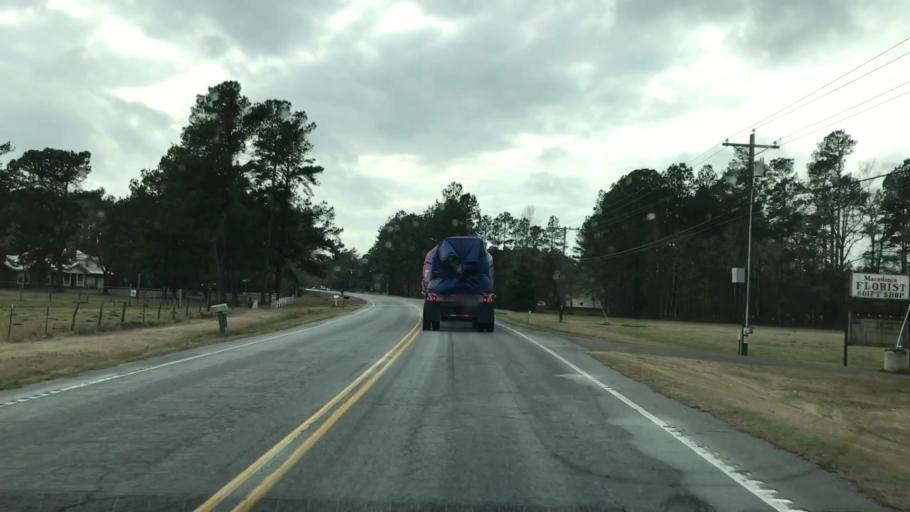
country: US
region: South Carolina
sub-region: Berkeley County
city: Bonneau Beach
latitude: 33.2811
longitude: -79.8821
